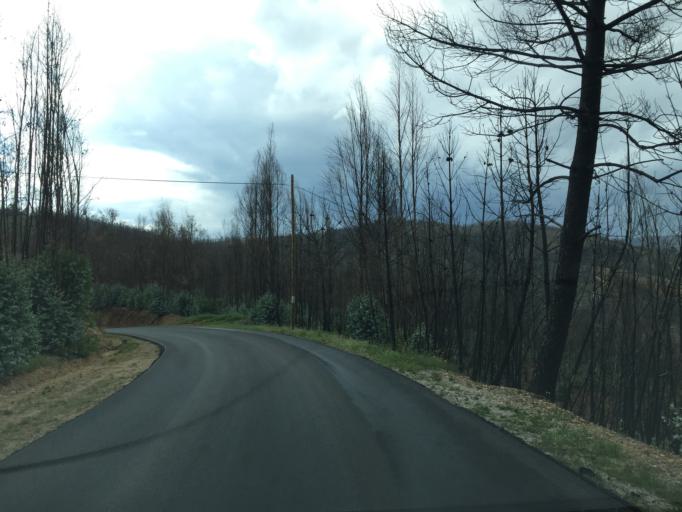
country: PT
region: Coimbra
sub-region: Pampilhosa da Serra
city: Pampilhosa da Serra
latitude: 40.0585
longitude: -8.0078
